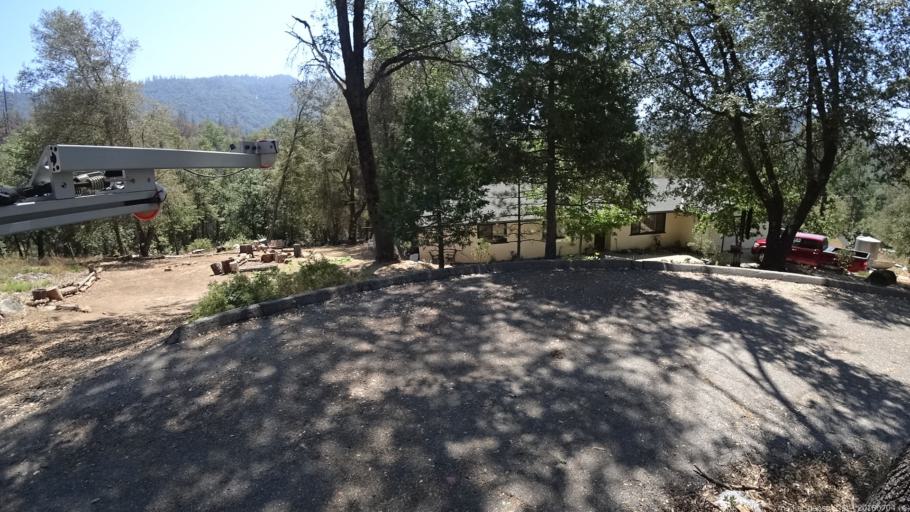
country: US
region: California
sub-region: Fresno County
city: Auberry
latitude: 37.2330
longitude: -119.4633
